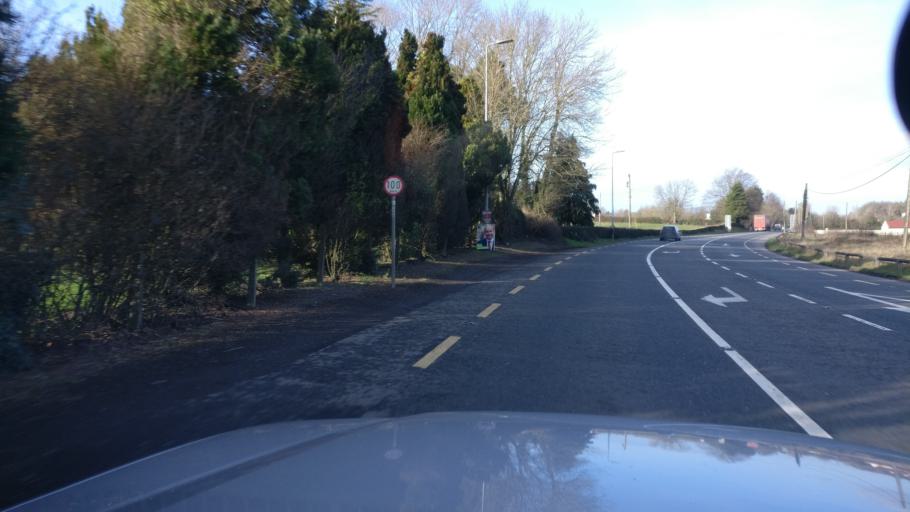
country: IE
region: Leinster
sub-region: Uibh Fhaili
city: Tullamore
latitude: 53.2218
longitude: -7.4756
